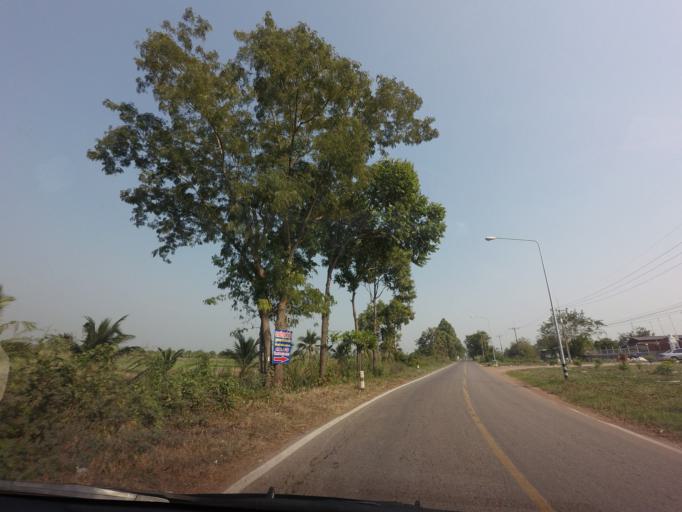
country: TH
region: Chachoengsao
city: Khlong Khuean
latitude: 13.8703
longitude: 101.1508
